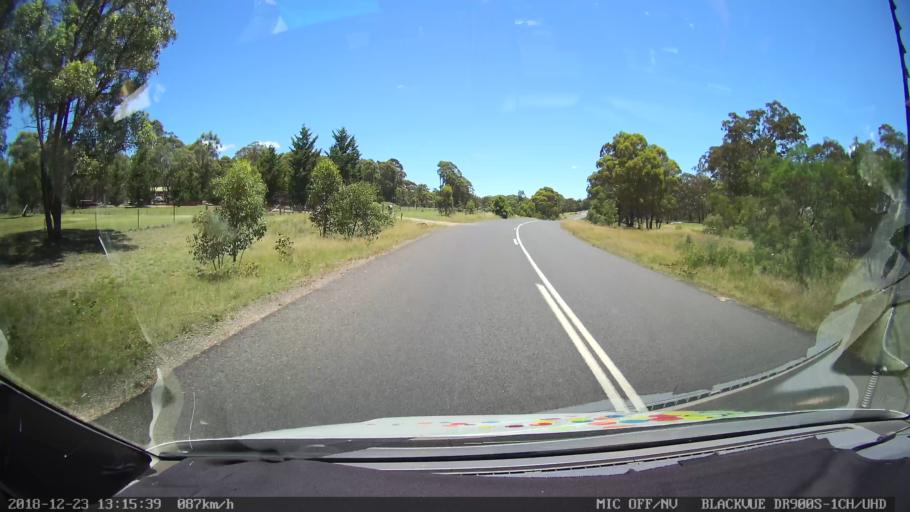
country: AU
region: New South Wales
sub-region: Armidale Dumaresq
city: Armidale
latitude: -30.5040
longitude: 151.5107
